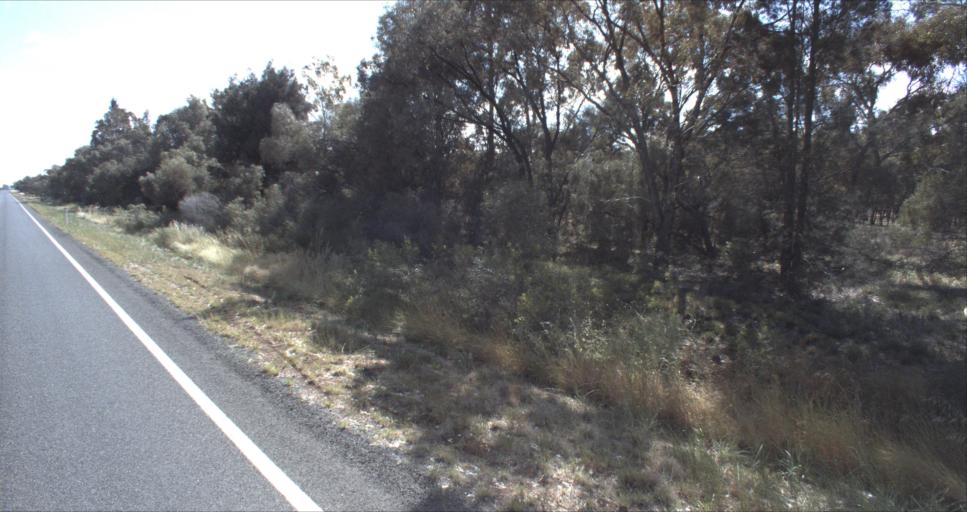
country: AU
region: New South Wales
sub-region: Murrumbidgee Shire
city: Darlington Point
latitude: -34.5300
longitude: 146.1741
